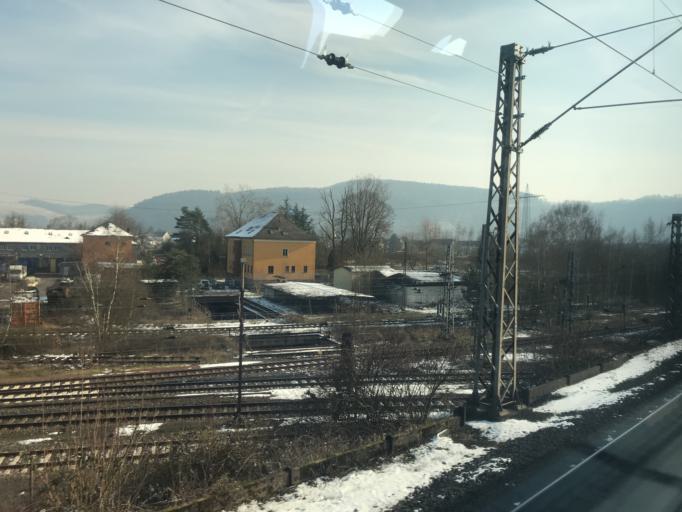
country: DE
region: Rheinland-Pfalz
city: Kenn
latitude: 49.7846
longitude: 6.6805
